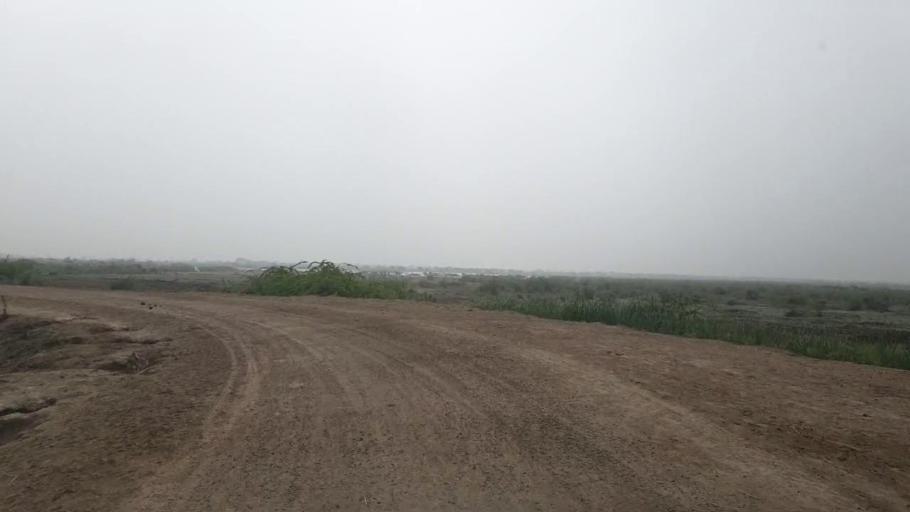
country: PK
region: Sindh
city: Badin
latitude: 24.5811
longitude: 68.6808
